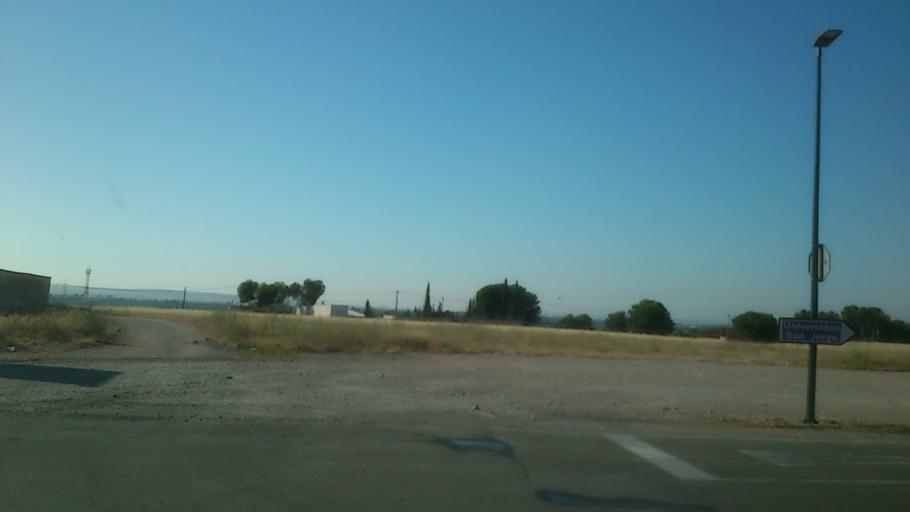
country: ES
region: Aragon
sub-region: Provincia de Zaragoza
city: Villanueva de Gallego
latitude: 41.7619
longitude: -0.8302
